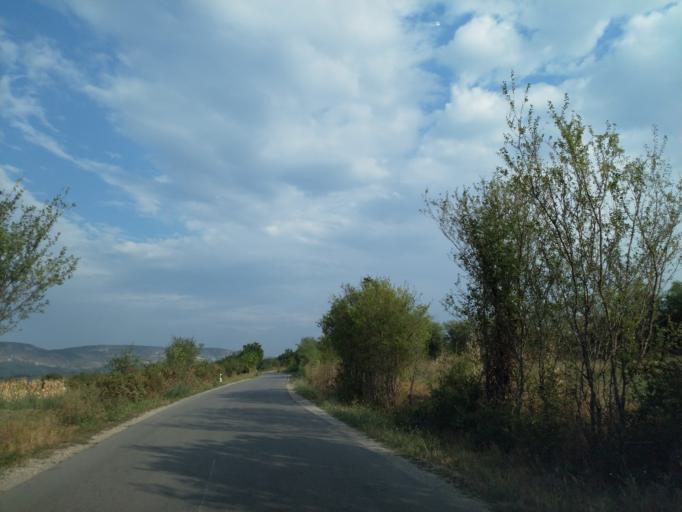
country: RS
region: Central Serbia
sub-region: Pomoravski Okrug
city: Paracin
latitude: 43.8433
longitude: 21.4872
